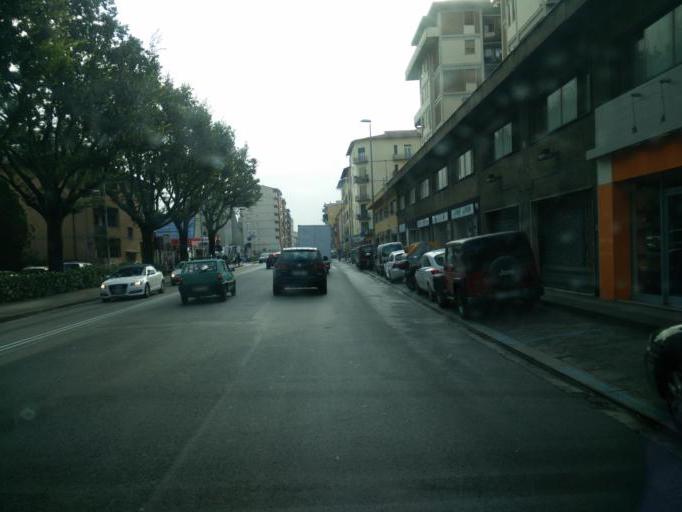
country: IT
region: Tuscany
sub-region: Province of Florence
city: Florence
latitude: 43.7931
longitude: 11.2131
